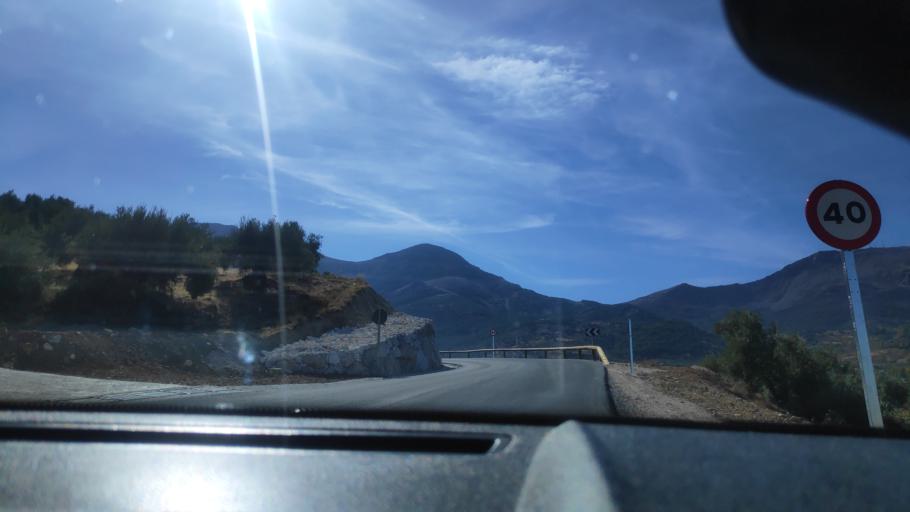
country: ES
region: Andalusia
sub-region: Provincia de Jaen
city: Torres
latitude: 37.7757
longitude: -3.4997
